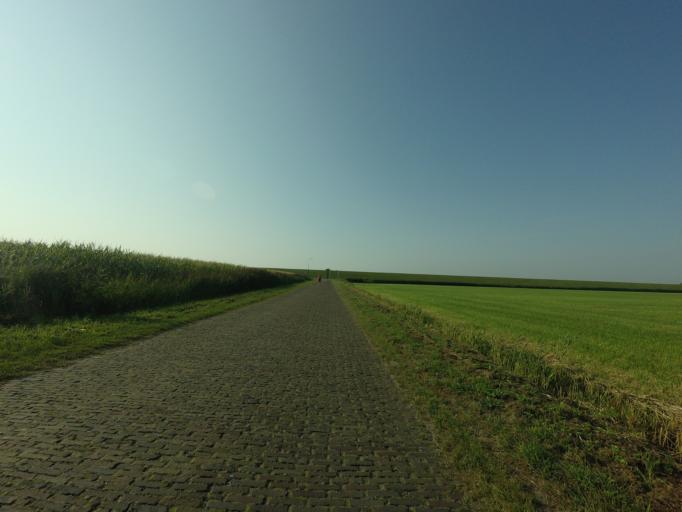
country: NL
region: Friesland
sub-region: Gemeente Schiermonnikoog
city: Schiermonnikoog
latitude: 53.4736
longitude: 6.1616
